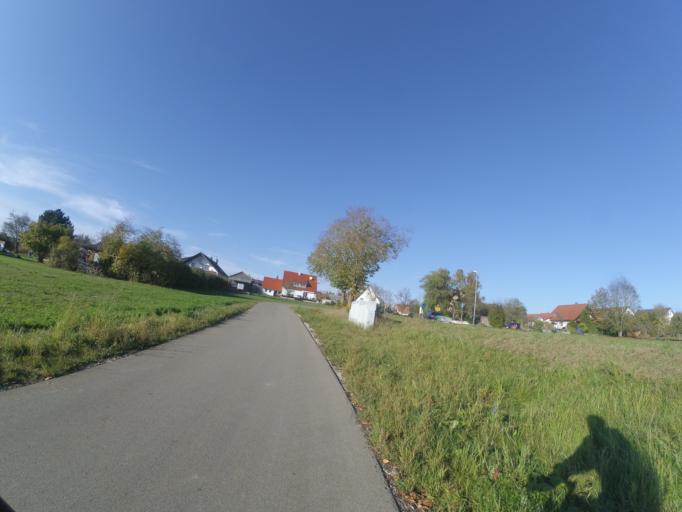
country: DE
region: Baden-Wuerttemberg
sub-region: Tuebingen Region
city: Blaubeuren
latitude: 48.4338
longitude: 9.8183
